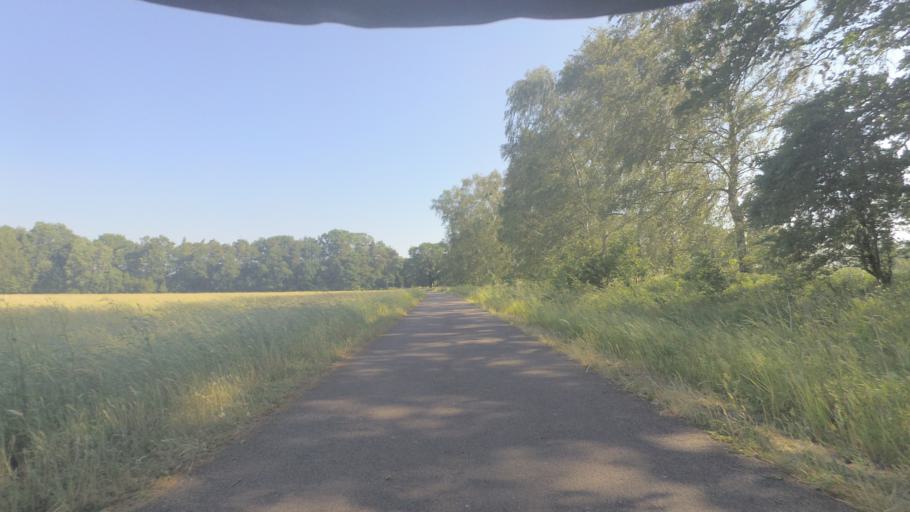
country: DE
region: Saxony-Anhalt
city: Rodleben
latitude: 51.8337
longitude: 12.1671
